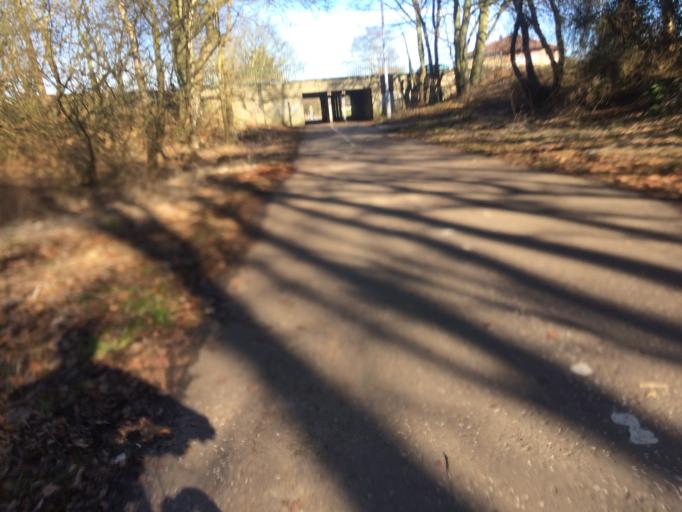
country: GB
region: Scotland
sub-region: Fife
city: Glenrothes
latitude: 56.1905
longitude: -3.1599
